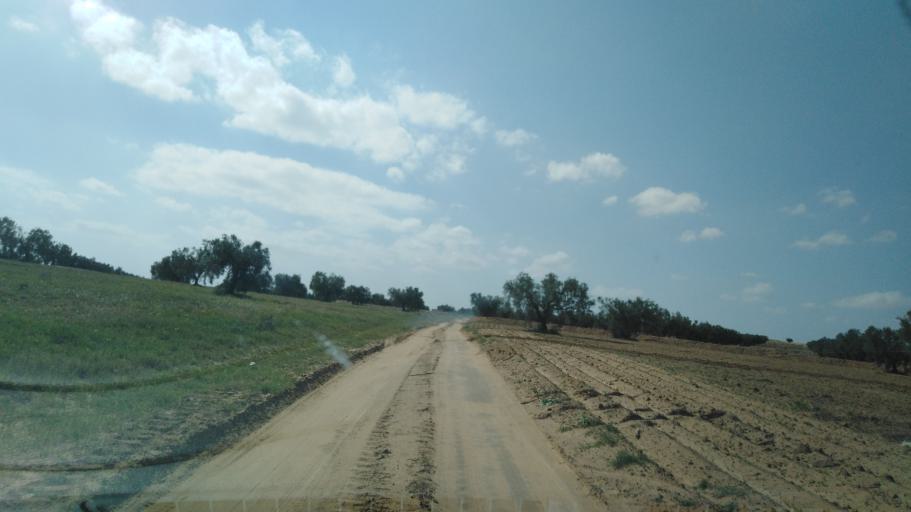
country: TN
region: Safaqis
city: Bi'r `Ali Bin Khalifah
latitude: 34.7926
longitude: 10.3994
